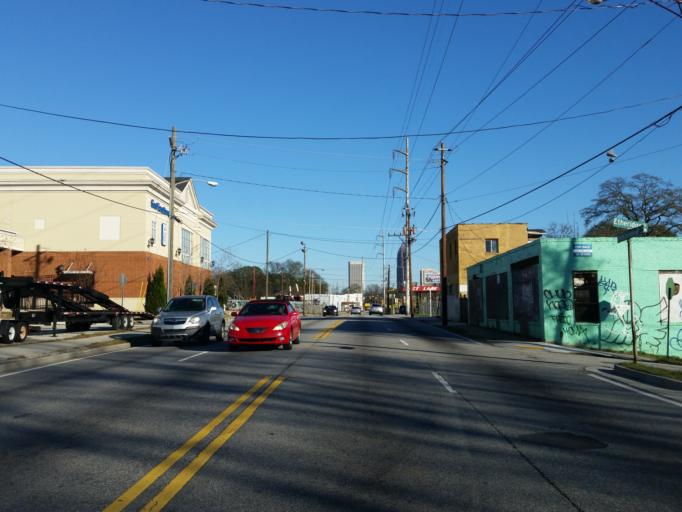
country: US
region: Georgia
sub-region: Fulton County
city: Atlanta
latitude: 33.7732
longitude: -84.4214
